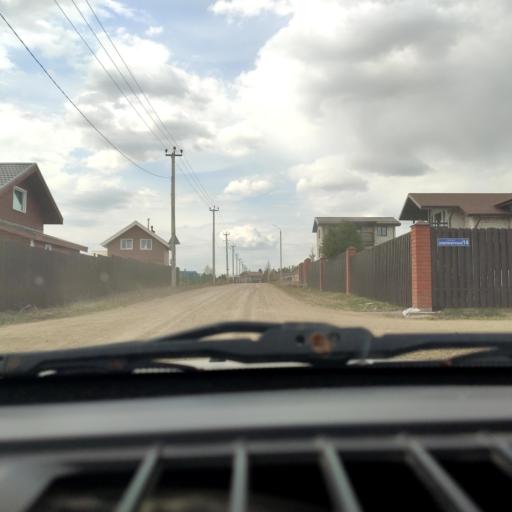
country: RU
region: Perm
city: Polazna
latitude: 58.3532
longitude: 56.2729
